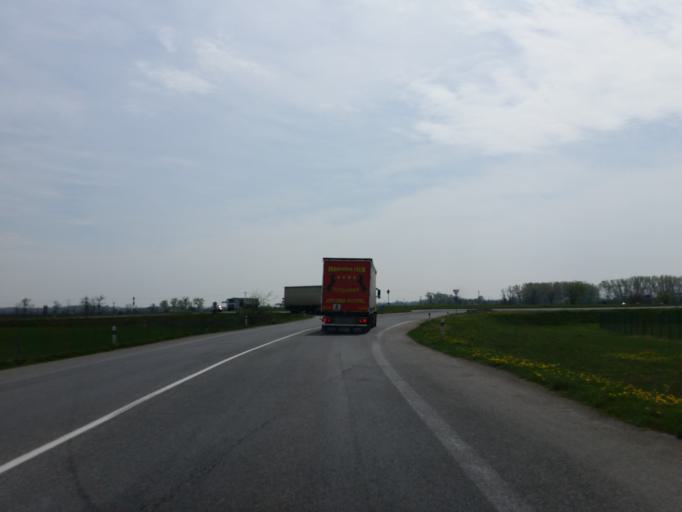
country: SK
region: Trnavsky
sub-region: Okres Galanta
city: Galanta
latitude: 48.2305
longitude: 17.7313
